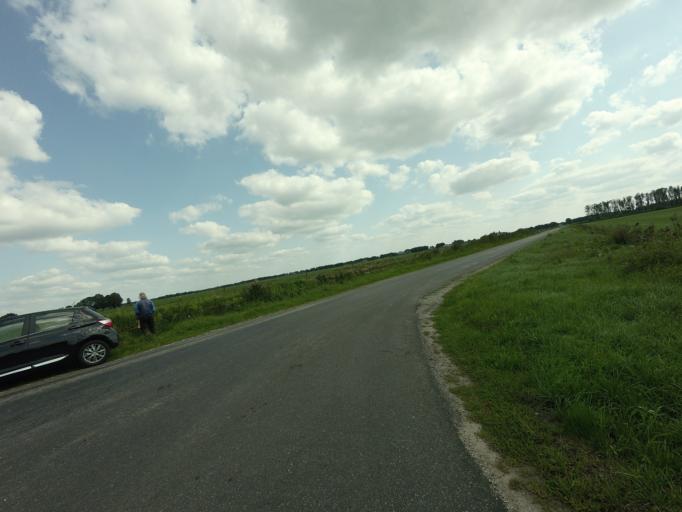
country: NL
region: Drenthe
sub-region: Gemeente Westerveld
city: Dwingeloo
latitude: 52.8832
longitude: 6.4233
